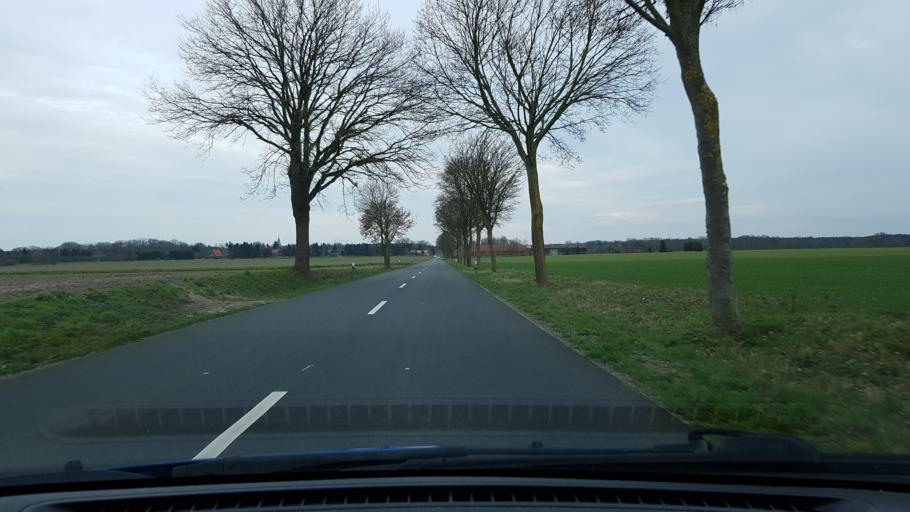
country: DE
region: Lower Saxony
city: Emmendorf
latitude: 53.0138
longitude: 10.5995
